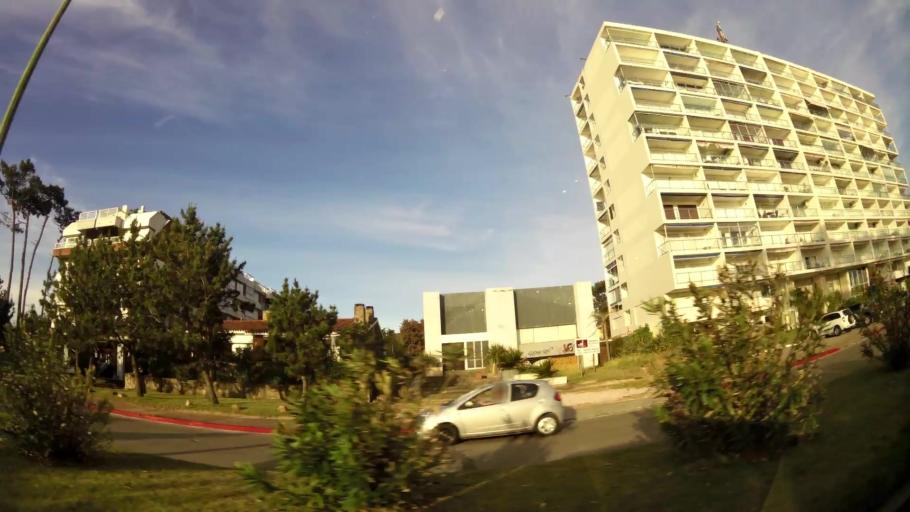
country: UY
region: Maldonado
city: Punta del Este
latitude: -34.9390
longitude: -54.9488
